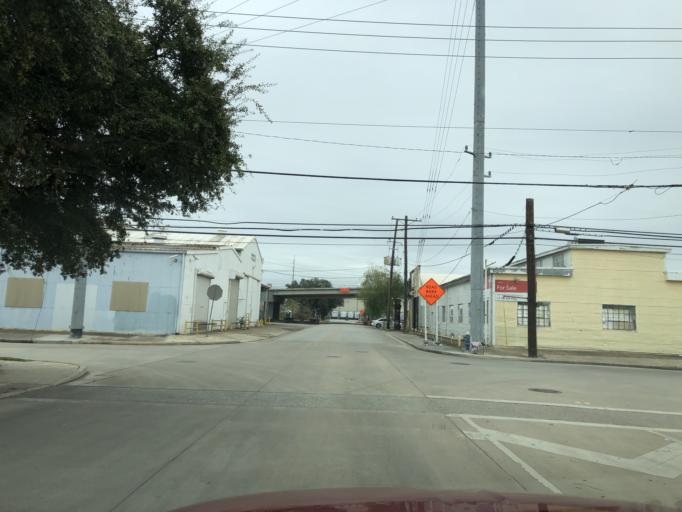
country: US
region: Texas
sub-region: Harris County
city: Houston
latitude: 29.7746
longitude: -95.3517
